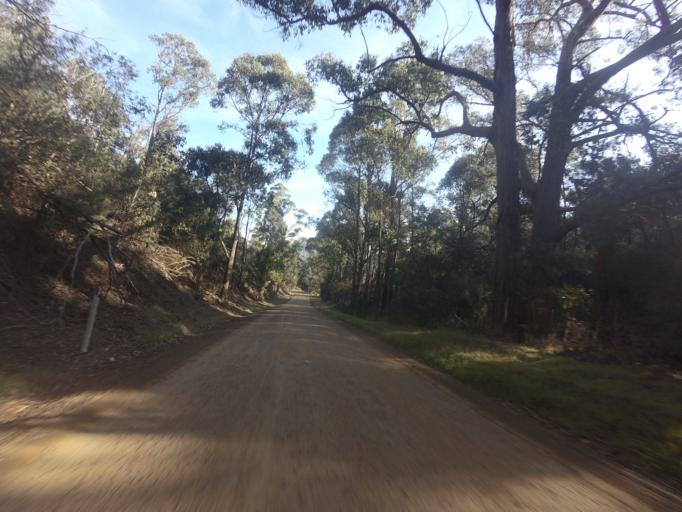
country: AU
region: Tasmania
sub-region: Sorell
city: Sorell
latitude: -42.4868
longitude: 147.4363
